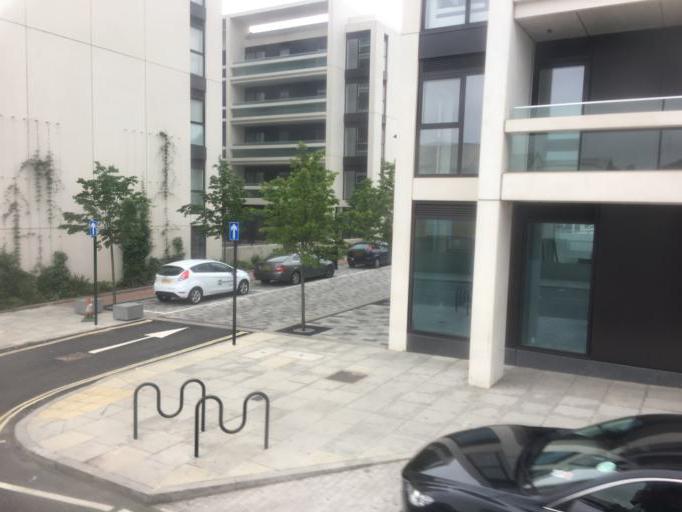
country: GB
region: England
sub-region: Greater London
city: Barnsbury
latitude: 51.5425
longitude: -0.1257
